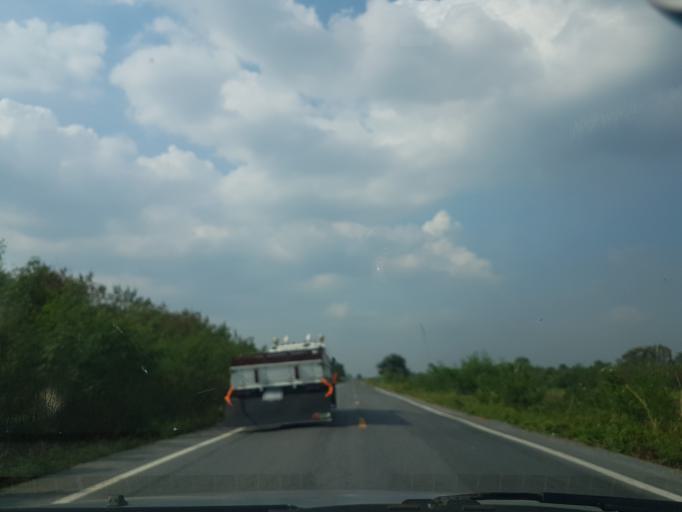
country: TH
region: Phra Nakhon Si Ayutthaya
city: Phachi
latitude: 14.4541
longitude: 100.7589
